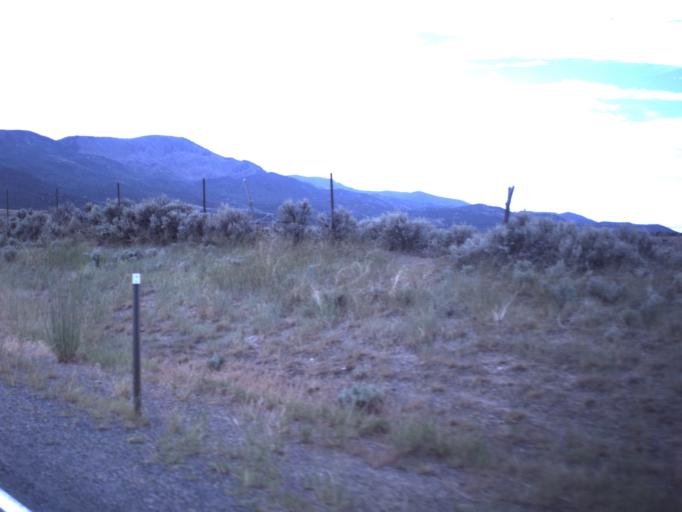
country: US
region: Utah
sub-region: Beaver County
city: Beaver
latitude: 38.6108
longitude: -112.6004
